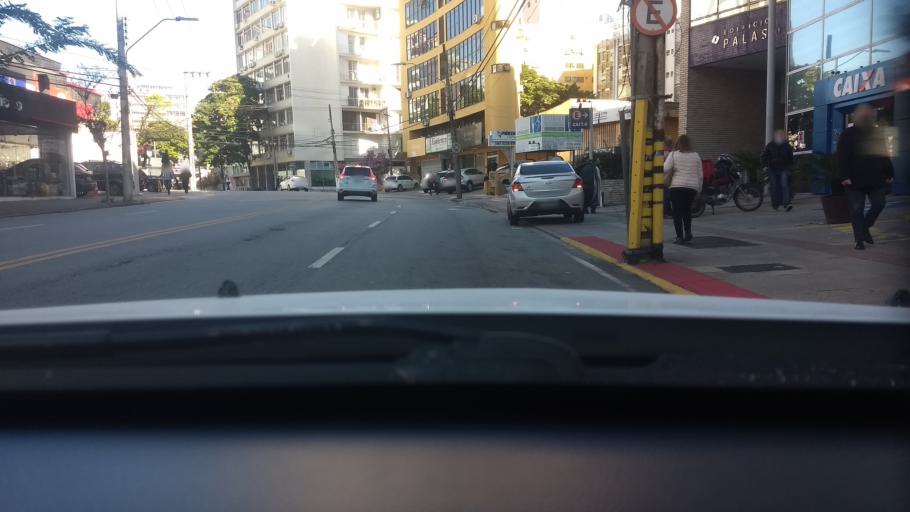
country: BR
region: Santa Catarina
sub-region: Florianopolis
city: Florianopolis
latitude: -27.5901
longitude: -48.5519
